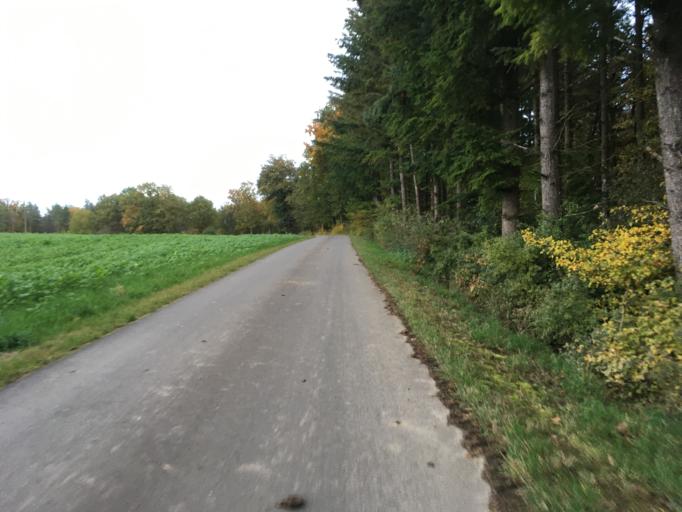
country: DE
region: Baden-Wuerttemberg
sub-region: Karlsruhe Region
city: Osterburken
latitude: 49.4702
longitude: 9.3931
